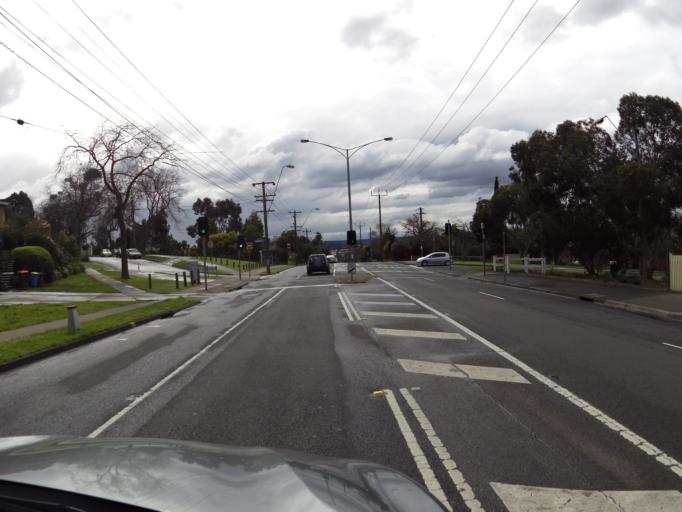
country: AU
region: Victoria
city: Balwyn
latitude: -37.8072
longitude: 145.0613
